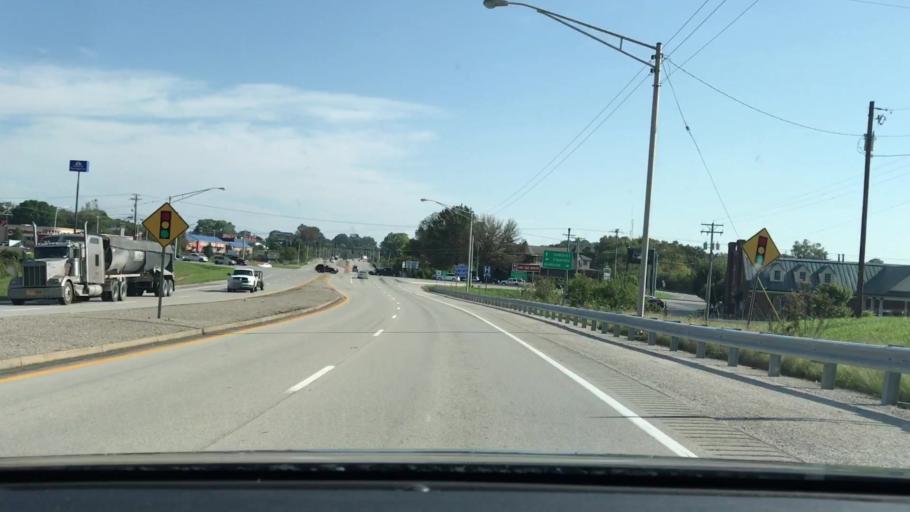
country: US
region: Kentucky
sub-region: Pulaski County
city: Somerset
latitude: 37.0938
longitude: -84.6212
